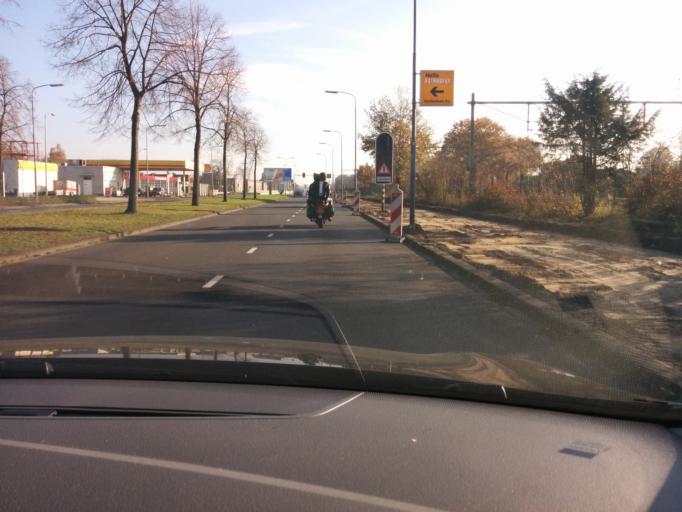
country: NL
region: North Brabant
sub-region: Gemeente Helmond
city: Helmond
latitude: 51.4764
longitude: 5.6695
